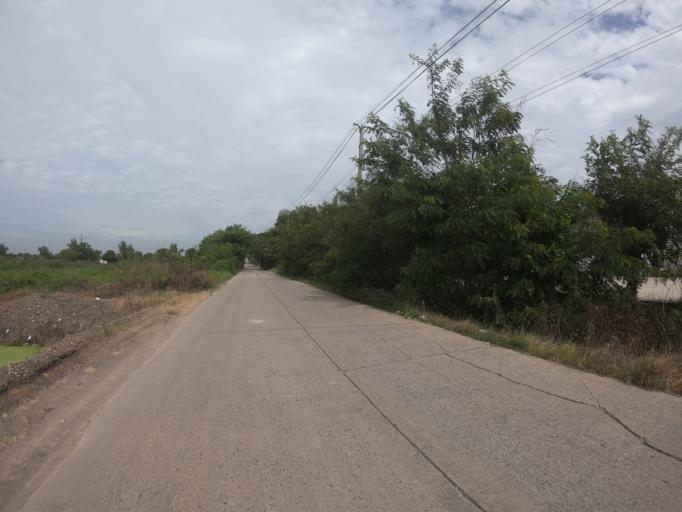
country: TH
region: Pathum Thani
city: Nong Suea
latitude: 14.0319
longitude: 100.8878
